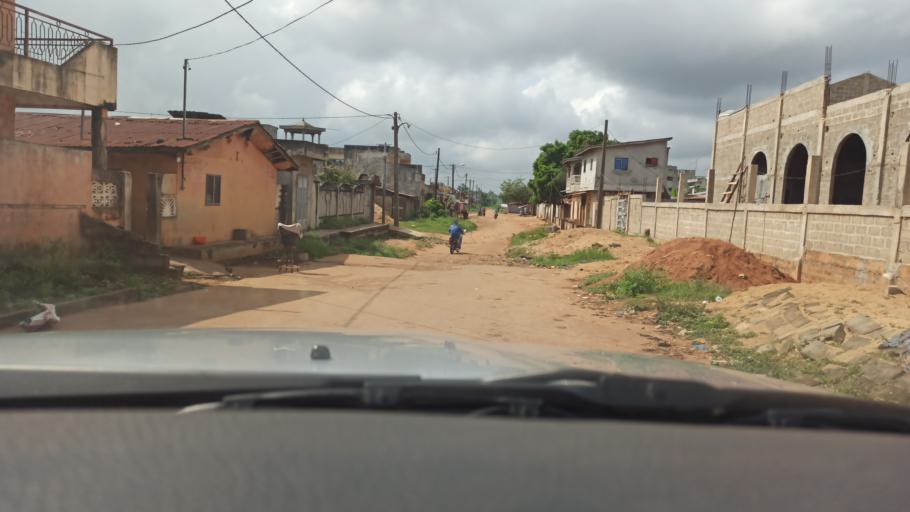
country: BJ
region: Queme
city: Porto-Novo
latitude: 6.4680
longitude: 2.6463
